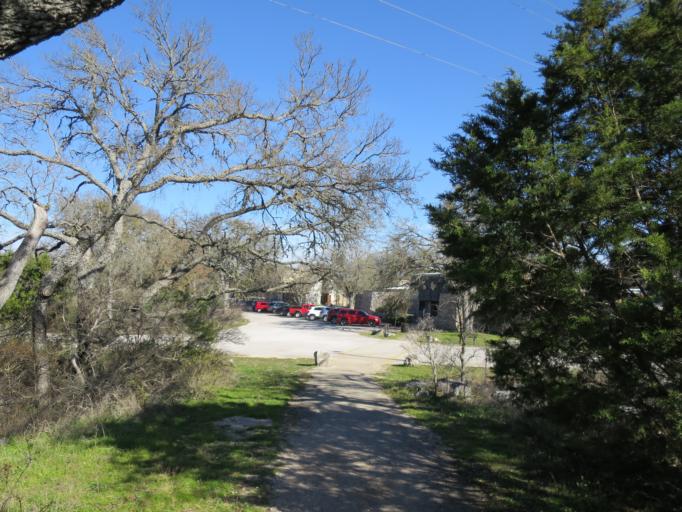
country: US
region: Texas
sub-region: Llano County
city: Kingsland
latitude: 30.6846
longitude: -98.3515
